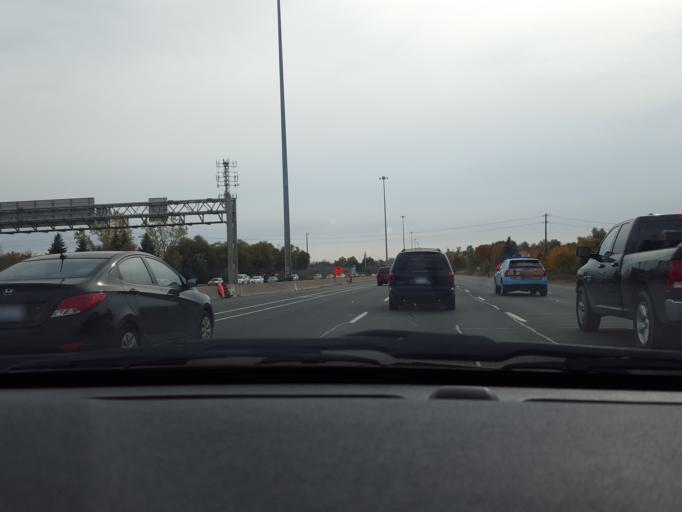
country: CA
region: Ontario
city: Willowdale
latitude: 43.8304
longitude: -79.3651
